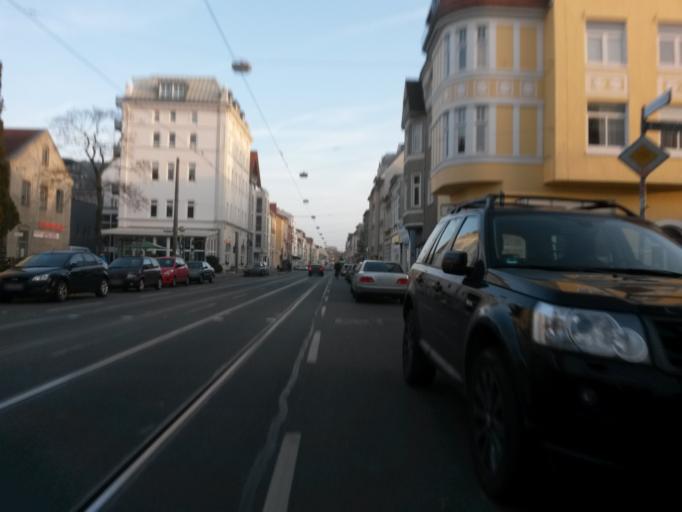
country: DE
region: Bremen
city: Bremen
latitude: 53.0658
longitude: 8.8053
